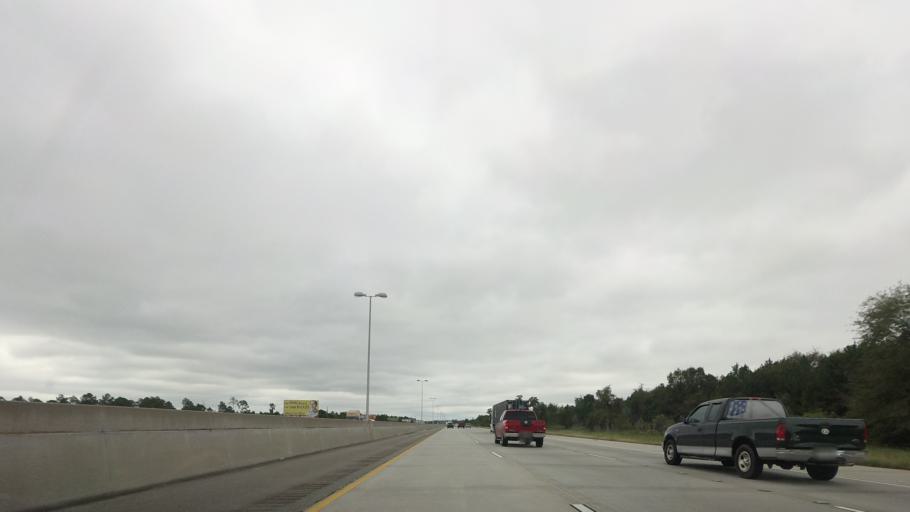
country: US
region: Georgia
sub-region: Cook County
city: Adel
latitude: 31.0792
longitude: -83.4103
